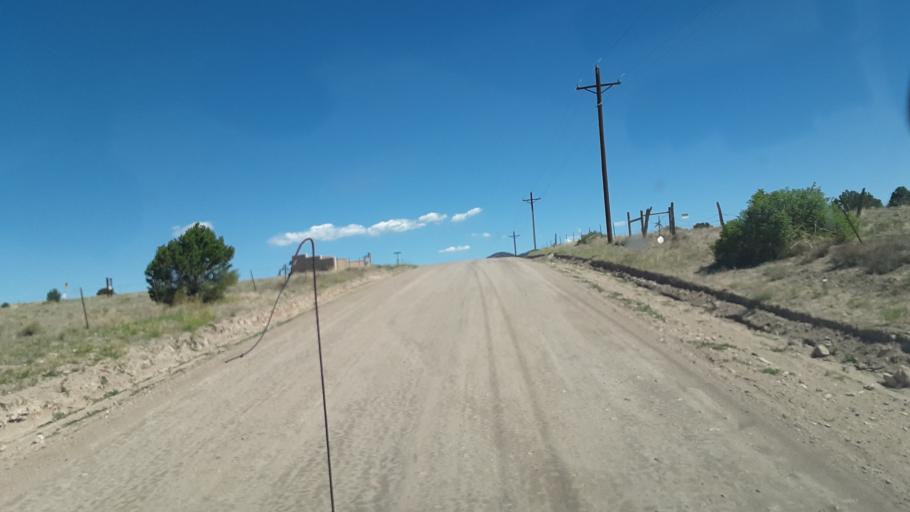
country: US
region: Colorado
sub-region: Custer County
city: Westcliffe
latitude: 38.2769
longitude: -105.5009
